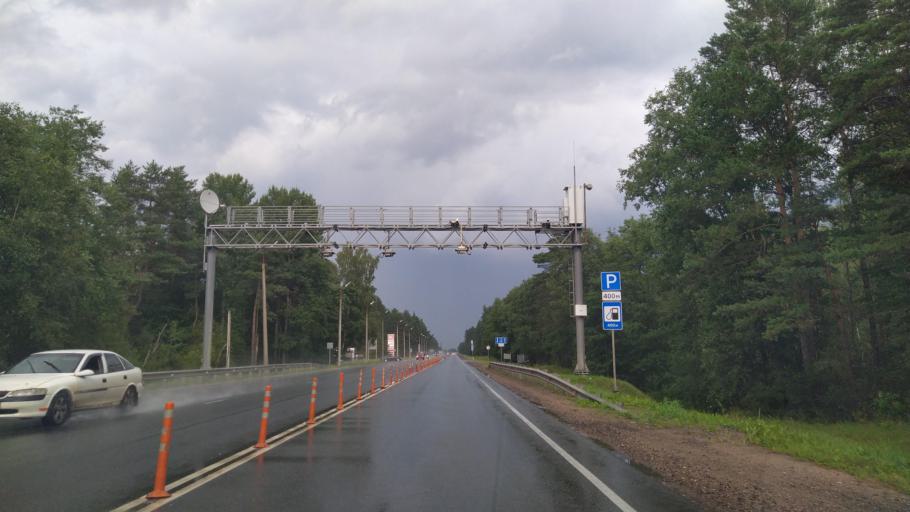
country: RU
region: Pskov
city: Pskov
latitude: 57.7311
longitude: 28.3578
